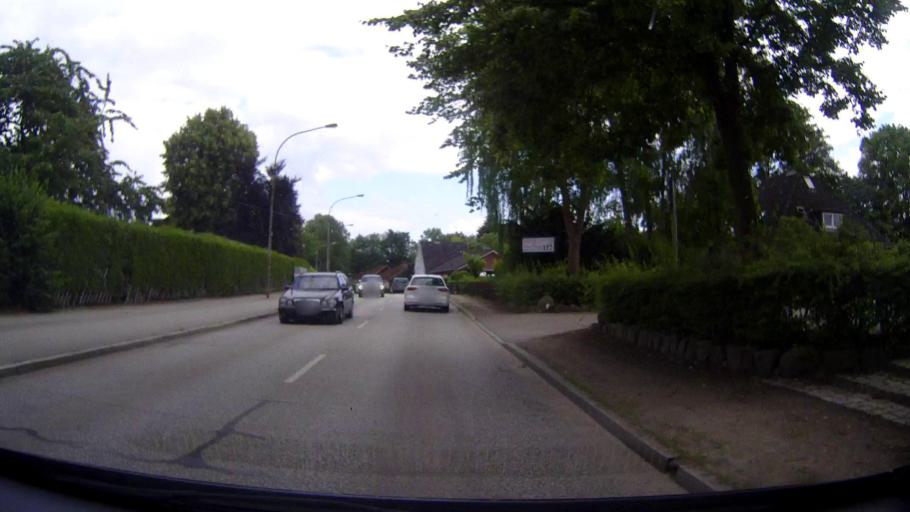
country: DE
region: Schleswig-Holstein
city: Luebeck
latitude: 53.8434
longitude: 10.6458
